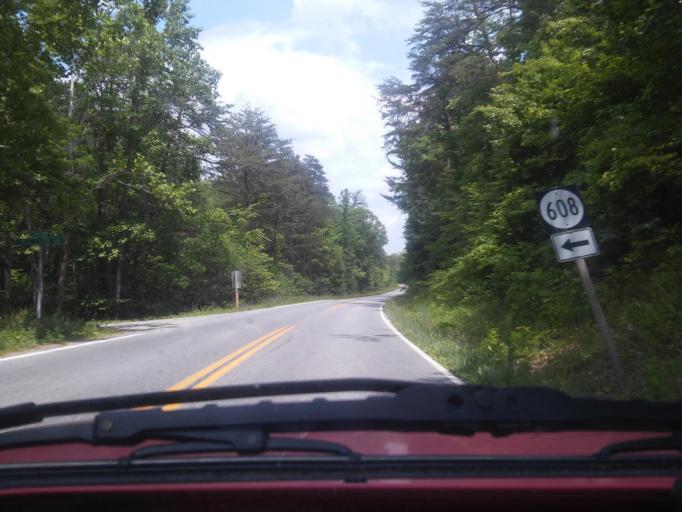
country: US
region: Virginia
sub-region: Craig County
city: New Castle
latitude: 37.5600
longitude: -80.0470
